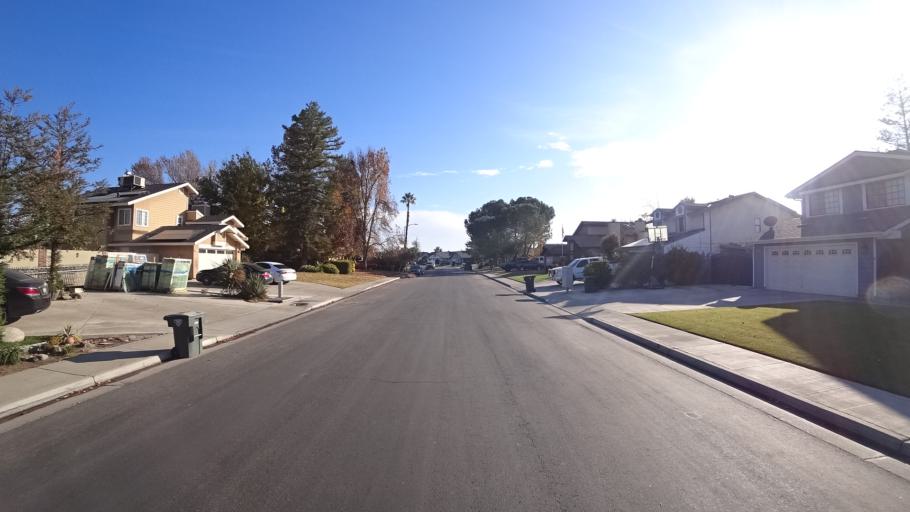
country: US
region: California
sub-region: Kern County
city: Rosedale
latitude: 35.3478
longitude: -119.1488
